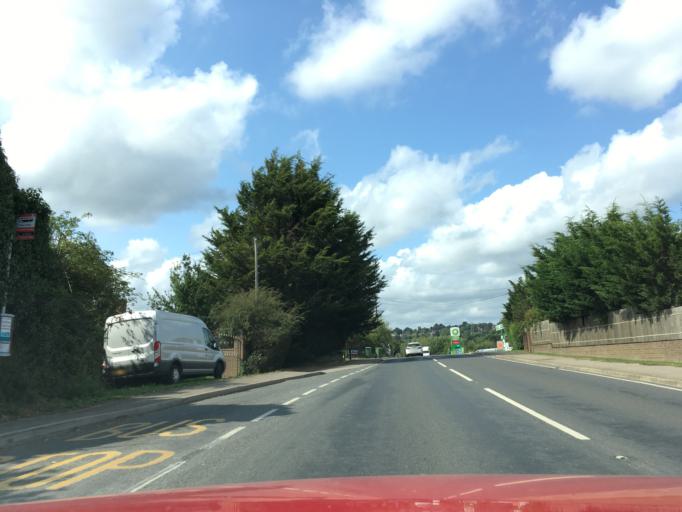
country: GB
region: England
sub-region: Kent
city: Headcorn
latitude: 51.1999
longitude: 0.5949
